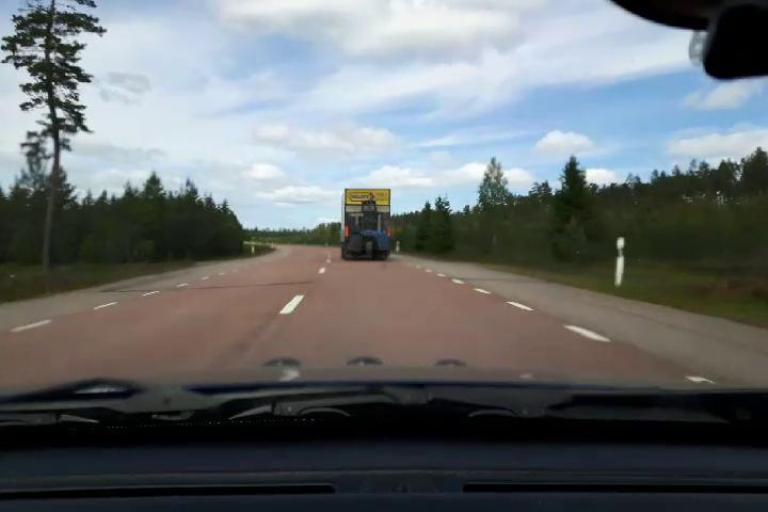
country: SE
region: Uppsala
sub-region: Osthammars Kommun
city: Bjorklinge
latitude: 60.1659
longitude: 17.4913
